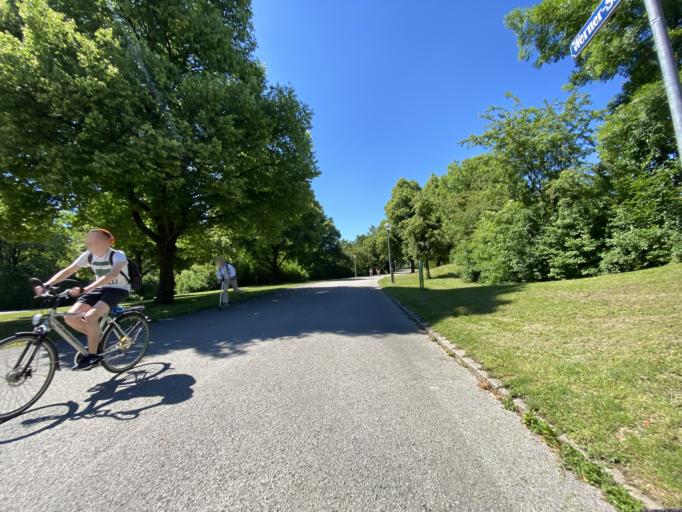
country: DE
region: Bavaria
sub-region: Upper Bavaria
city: Munich
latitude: 48.1773
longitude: 11.5429
